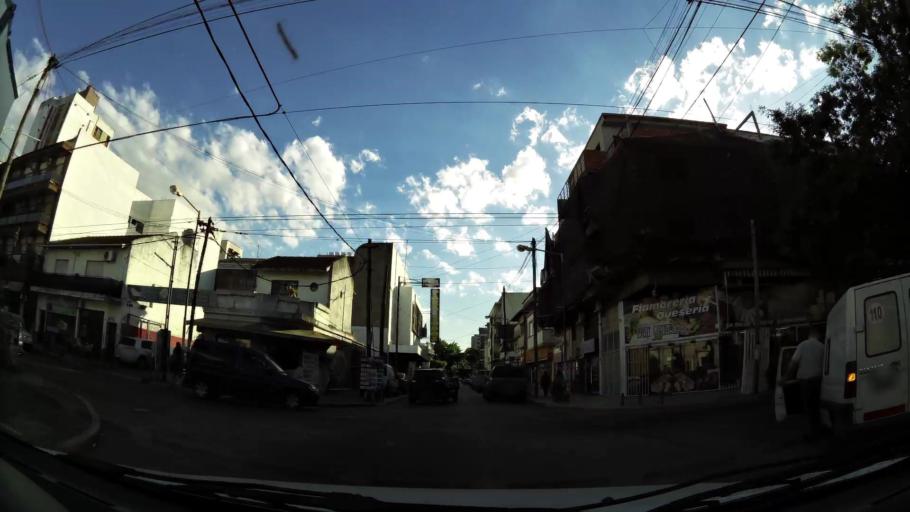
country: AR
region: Buenos Aires
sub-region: Partido de General San Martin
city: General San Martin
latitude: -34.5525
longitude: -58.5564
